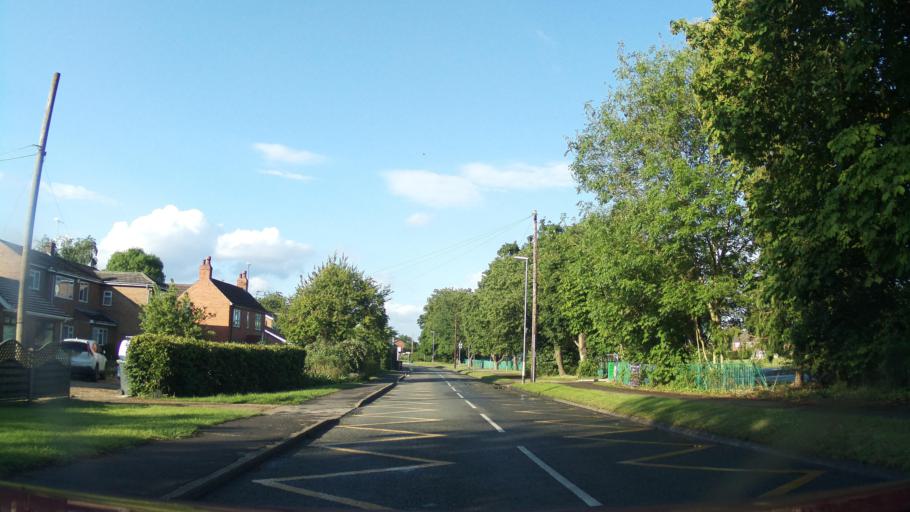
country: GB
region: England
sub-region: Lincolnshire
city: Skellingthorpe
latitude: 53.1282
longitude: -0.6392
